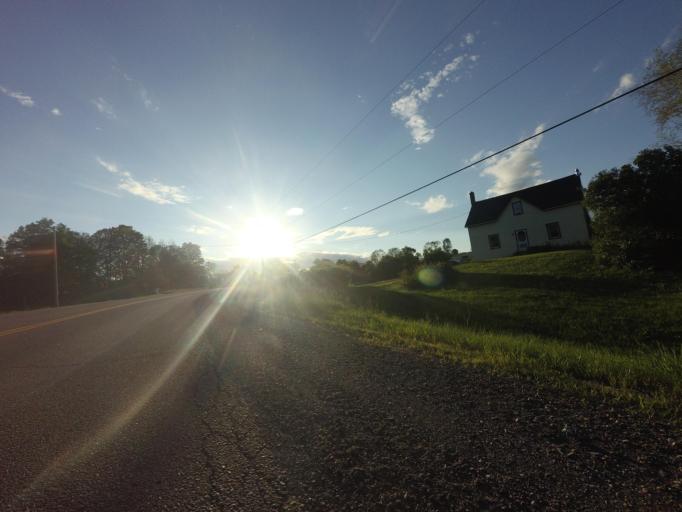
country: CA
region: Ontario
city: Renfrew
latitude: 45.3681
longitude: -76.5533
